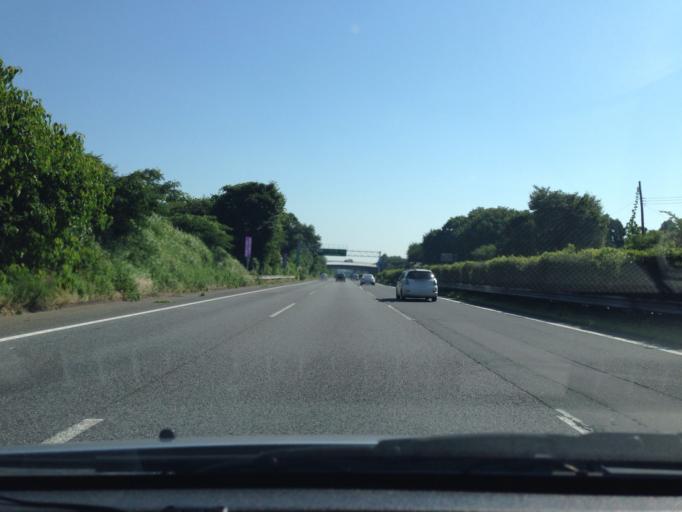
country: JP
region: Ibaraki
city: Ishioka
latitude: 36.1582
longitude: 140.2269
